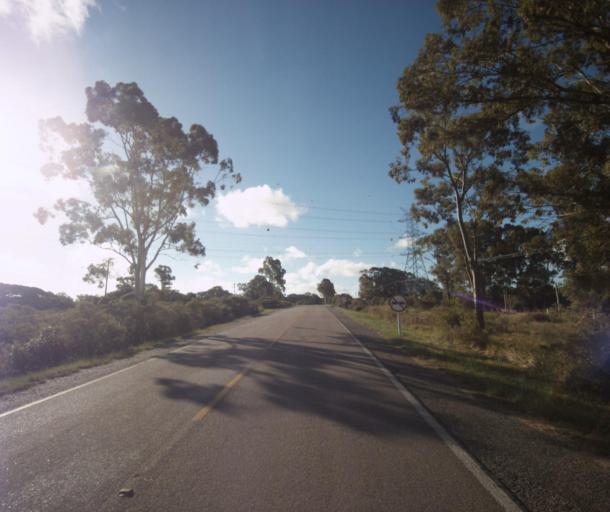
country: BR
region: Rio Grande do Sul
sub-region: Arroio Grande
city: Arroio Grande
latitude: -32.4998
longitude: -52.5755
